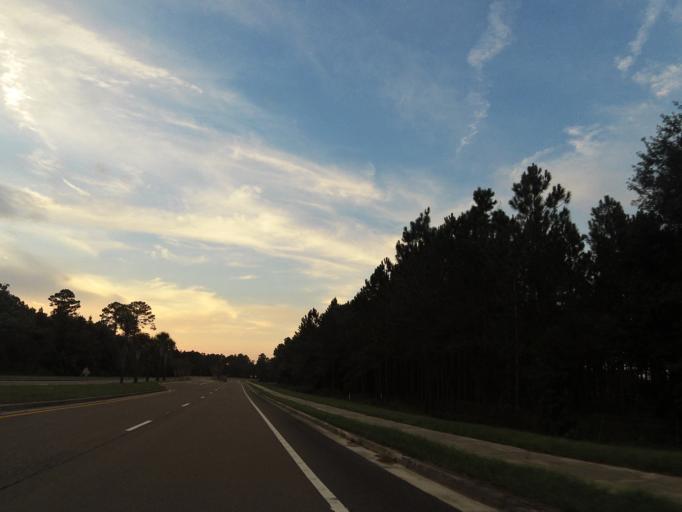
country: US
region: Florida
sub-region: Saint Johns County
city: Fruit Cove
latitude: 30.0988
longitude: -81.5387
